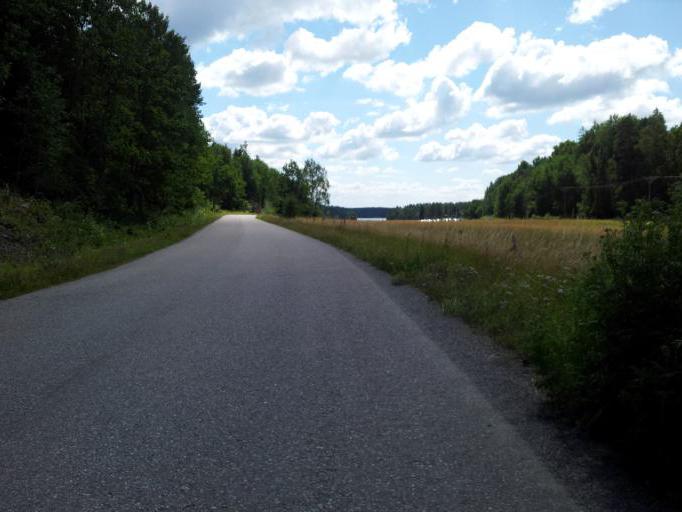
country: SE
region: Uppsala
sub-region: Knivsta Kommun
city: Knivsta
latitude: 59.8422
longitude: 17.9143
